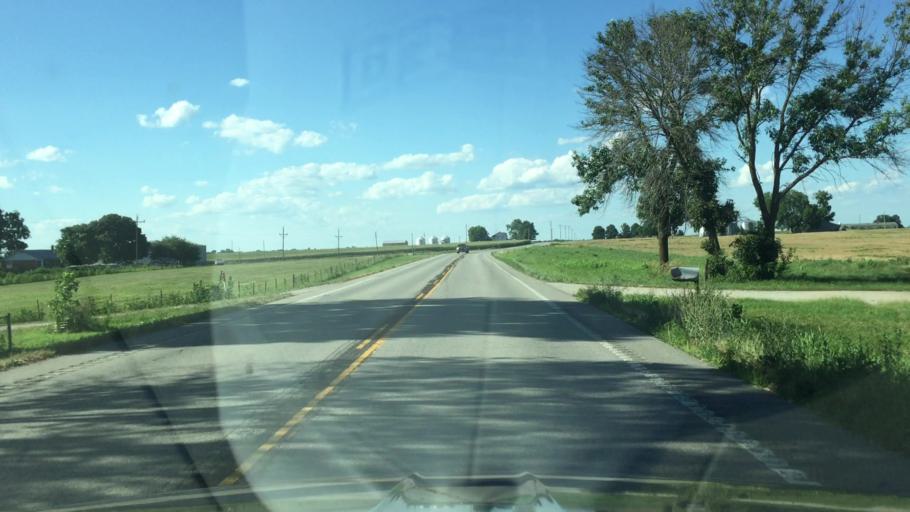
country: US
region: Missouri
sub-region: Moniteau County
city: Tipton
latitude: 38.6066
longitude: -92.7900
